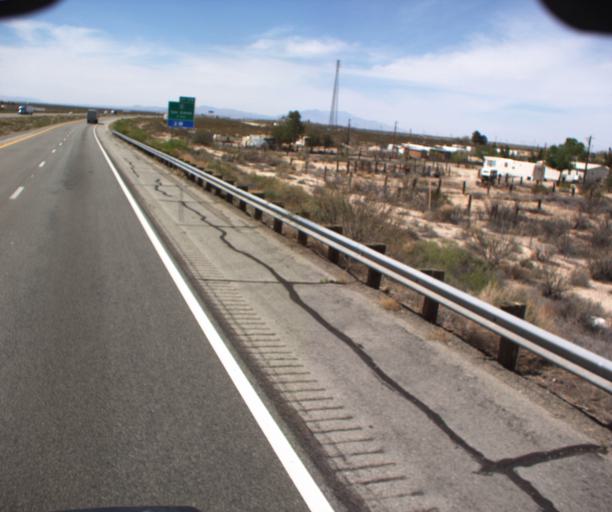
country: US
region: New Mexico
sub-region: Hidalgo County
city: Lordsburg
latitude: 32.2641
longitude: -109.2305
